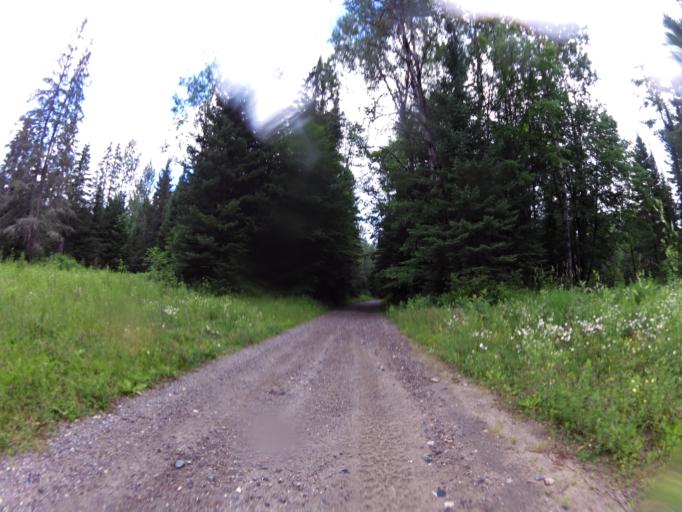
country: CA
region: Ontario
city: Renfrew
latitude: 45.0821
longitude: -76.7210
